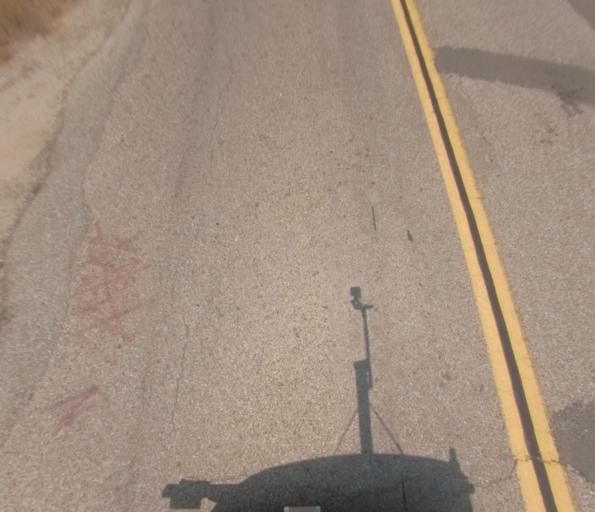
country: US
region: California
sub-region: Madera County
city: Ahwahnee
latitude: 37.3538
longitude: -119.7283
